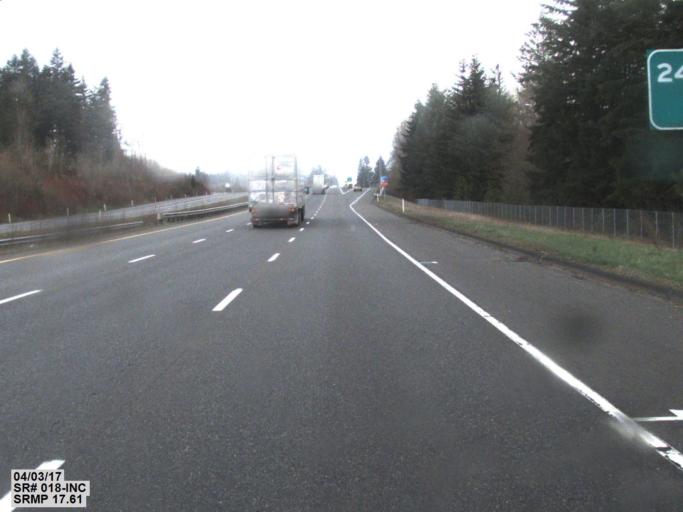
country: US
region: Washington
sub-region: King County
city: Maple Valley
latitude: 47.4129
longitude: -122.0229
